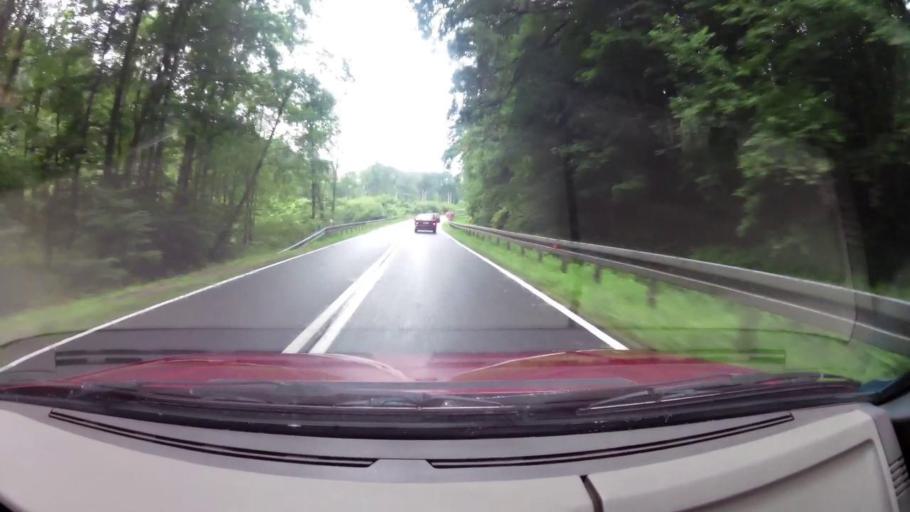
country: PL
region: West Pomeranian Voivodeship
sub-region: Powiat stargardzki
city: Marianowo
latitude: 53.4209
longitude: 15.2756
